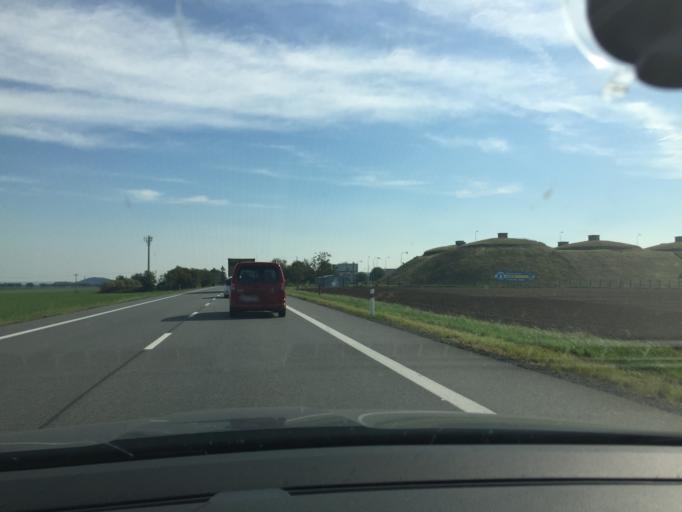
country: CZ
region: Central Bohemia
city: Cerhenice
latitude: 50.0457
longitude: 15.0690
